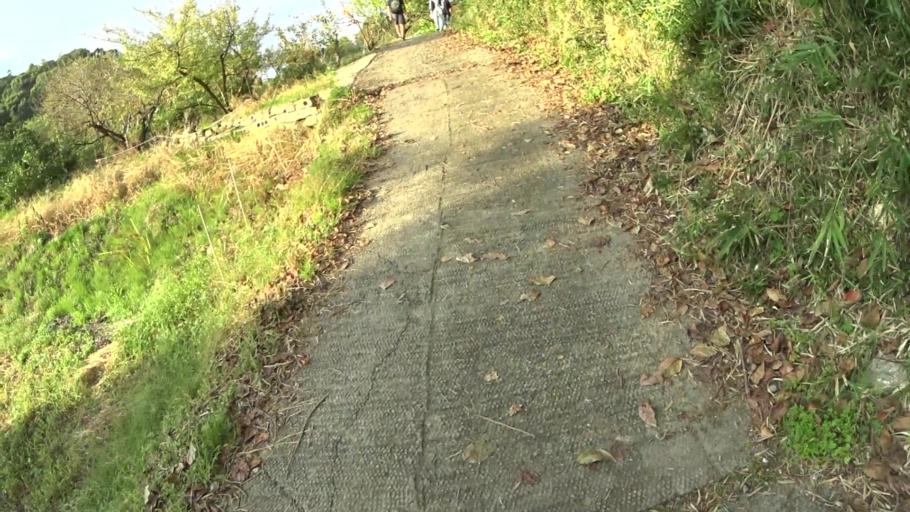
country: JP
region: Nara
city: Tenri
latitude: 34.5492
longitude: 135.8509
